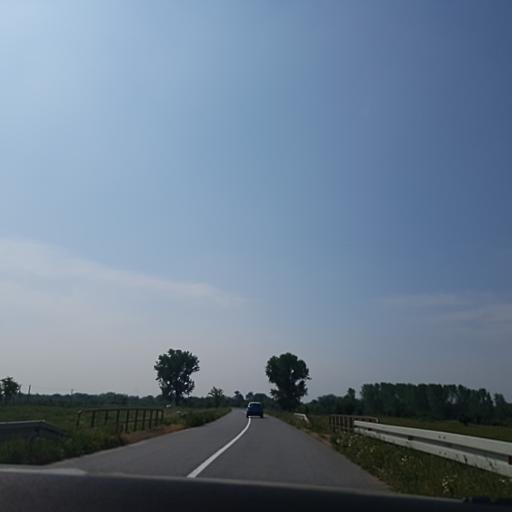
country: RS
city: Jarkovac
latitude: 45.2780
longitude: 20.7629
